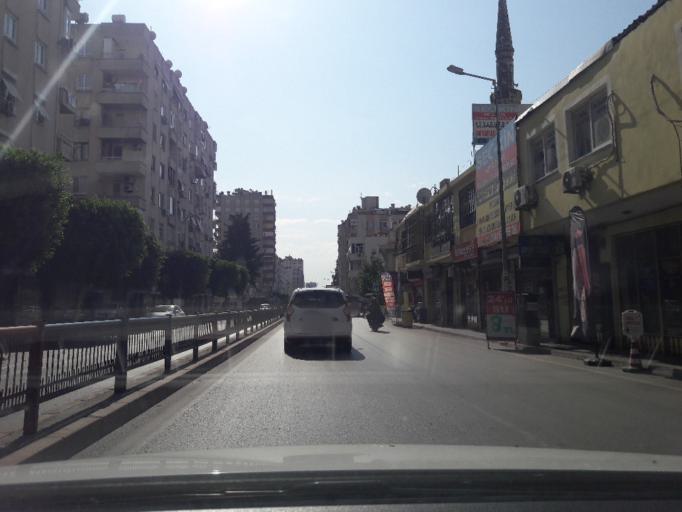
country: TR
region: Adana
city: Adana
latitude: 37.0123
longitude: 35.3228
